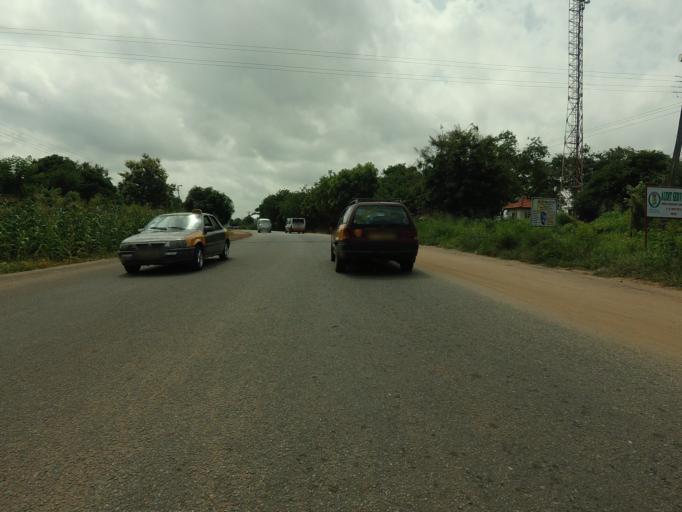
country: TG
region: Maritime
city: Lome
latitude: 6.1176
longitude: 1.1329
